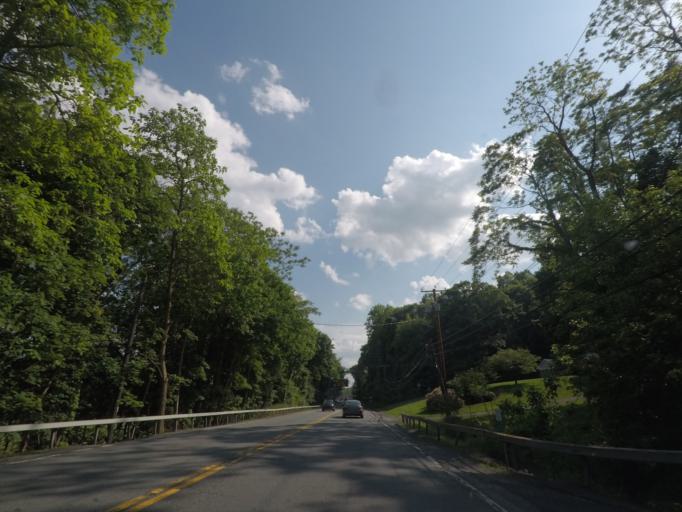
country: US
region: New York
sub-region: Orange County
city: Balmville
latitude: 41.5250
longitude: -74.0203
